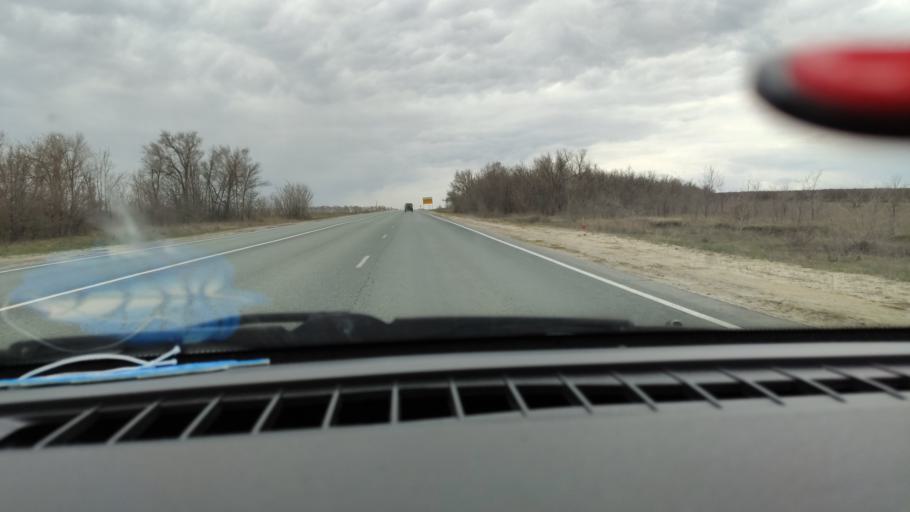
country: RU
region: Saratov
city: Sinodskoye
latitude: 51.9064
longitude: 46.5497
